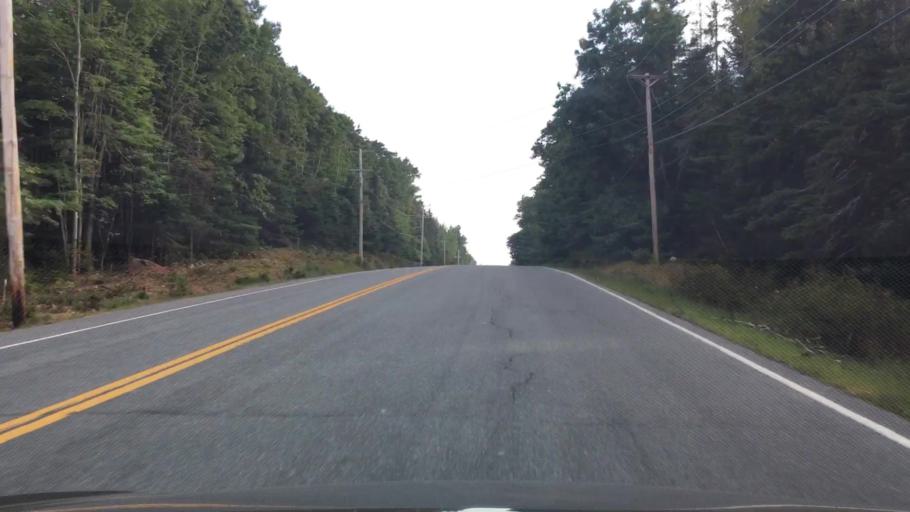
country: US
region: Maine
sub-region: Hancock County
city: Surry
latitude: 44.4896
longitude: -68.5102
